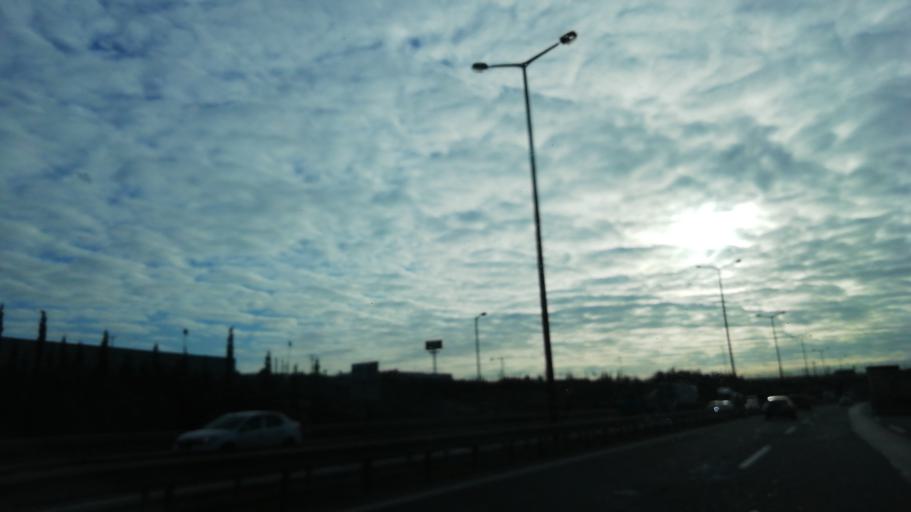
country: TR
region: Kocaeli
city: Balcik
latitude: 40.8724
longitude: 29.3939
